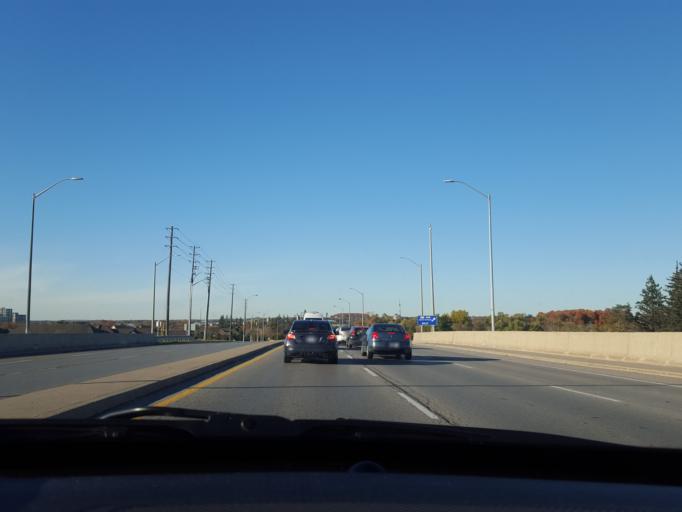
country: CA
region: Ontario
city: Markham
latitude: 43.8561
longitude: -79.2813
